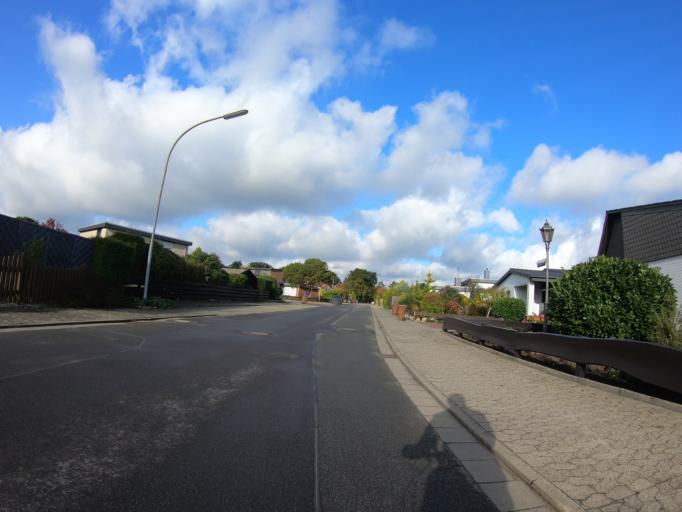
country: DE
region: Lower Saxony
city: Wagenhoff
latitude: 52.5175
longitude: 10.5430
